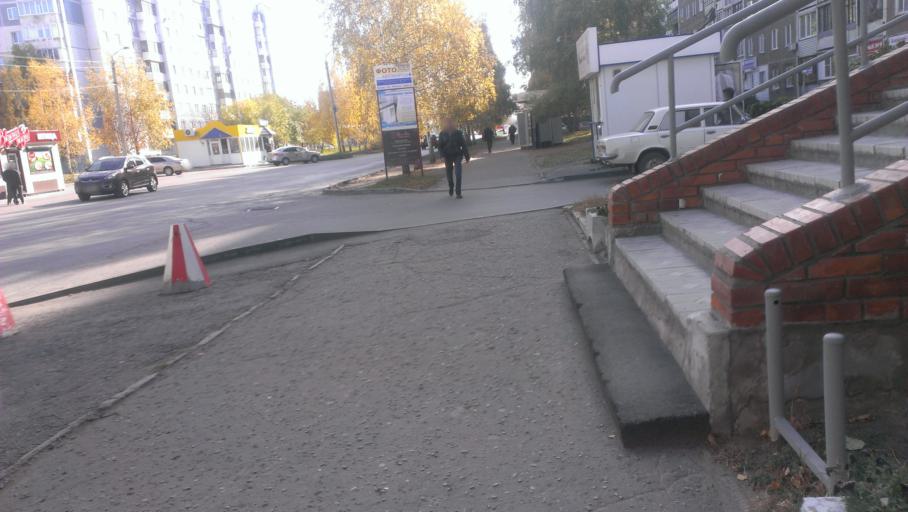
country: RU
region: Altai Krai
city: Novosilikatnyy
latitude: 53.3324
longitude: 83.6762
